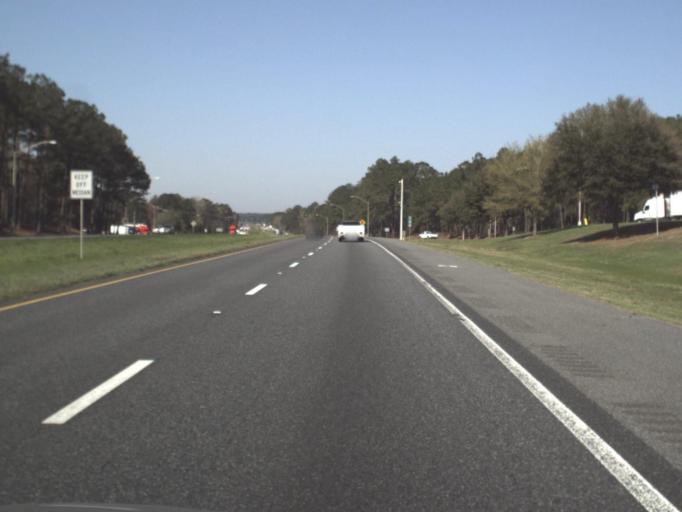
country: US
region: Florida
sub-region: Gadsden County
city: Midway
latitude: 30.4843
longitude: -84.3843
